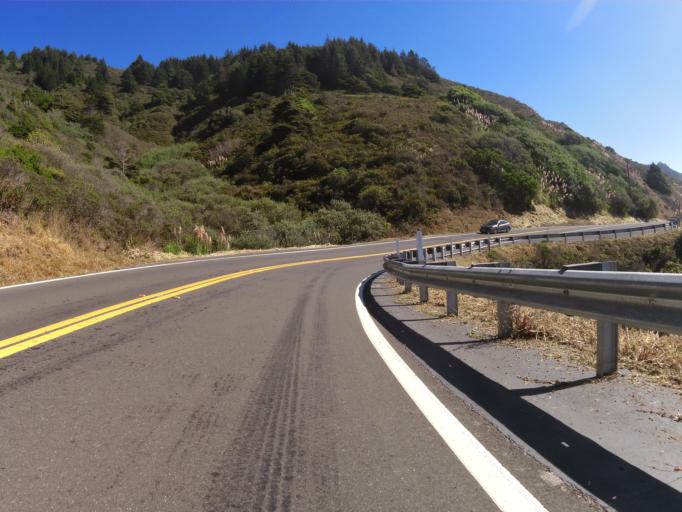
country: US
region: California
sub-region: Mendocino County
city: Fort Bragg
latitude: 39.6224
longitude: -123.7813
